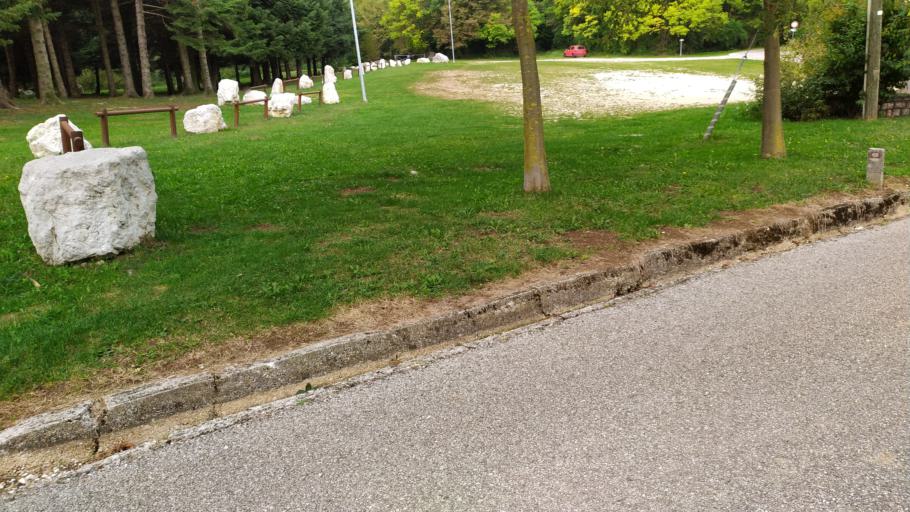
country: IT
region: Friuli Venezia Giulia
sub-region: Provincia di Pordenone
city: Marsure
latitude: 46.0889
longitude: 12.5731
